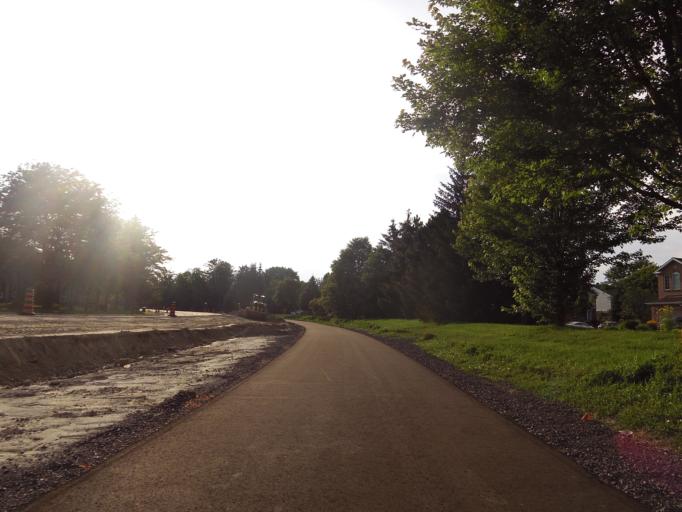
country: CA
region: Ontario
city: Bells Corners
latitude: 45.3154
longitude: -75.8867
